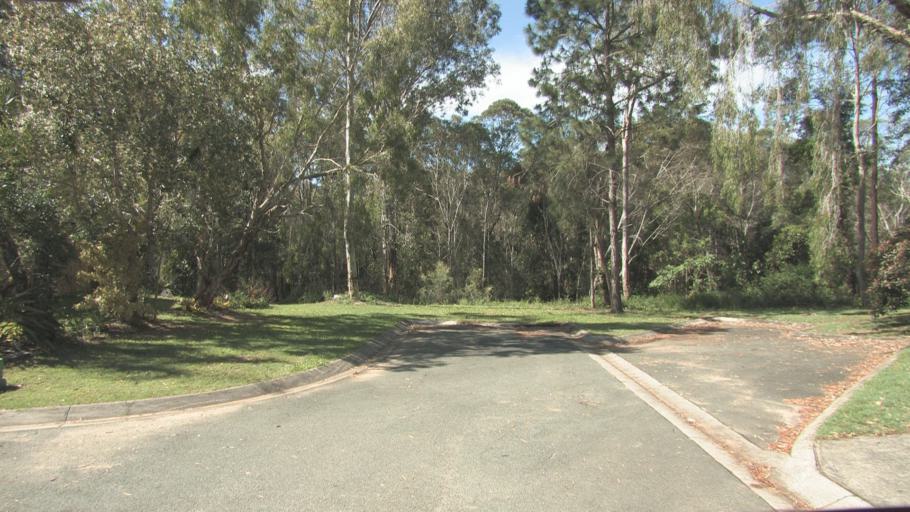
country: AU
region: Queensland
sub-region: Gold Coast
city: Yatala
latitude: -27.7008
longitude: 153.2194
